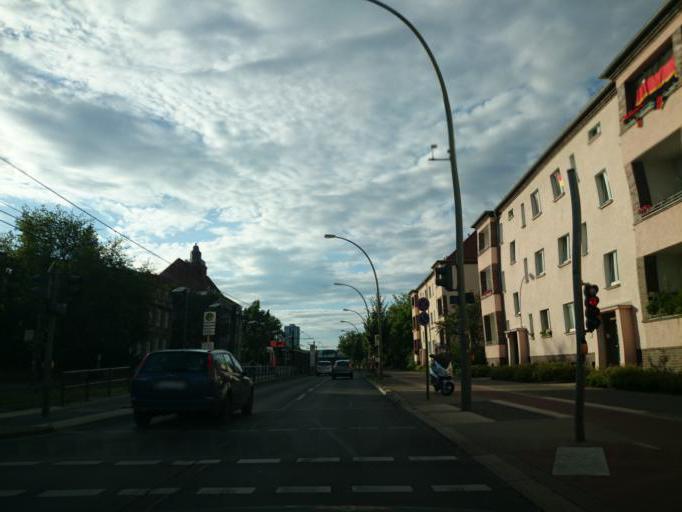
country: DE
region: Berlin
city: Karlshorst
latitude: 52.4921
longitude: 13.5272
